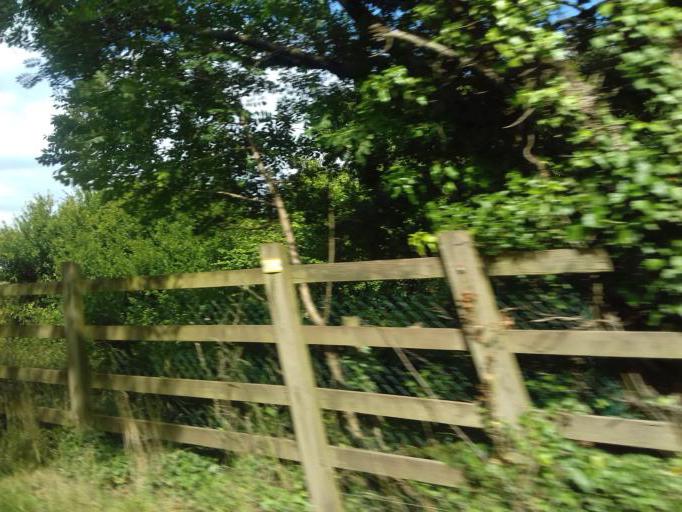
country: IE
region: Leinster
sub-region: Loch Garman
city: Loch Garman
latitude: 52.2956
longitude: -6.6430
